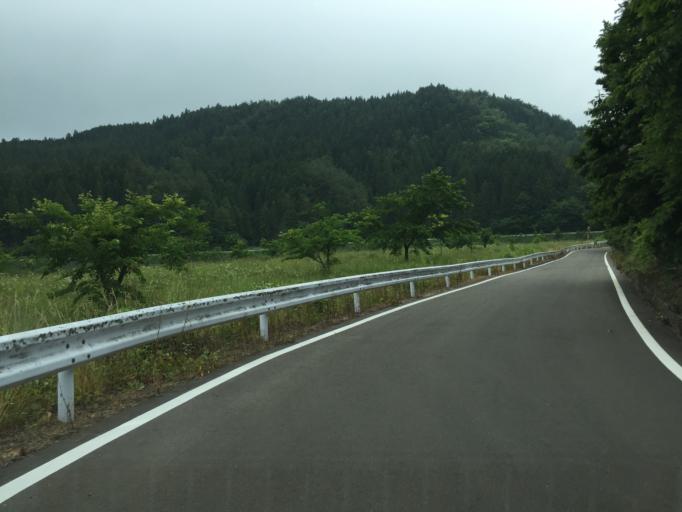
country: JP
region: Miyagi
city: Marumori
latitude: 37.7958
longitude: 140.7533
